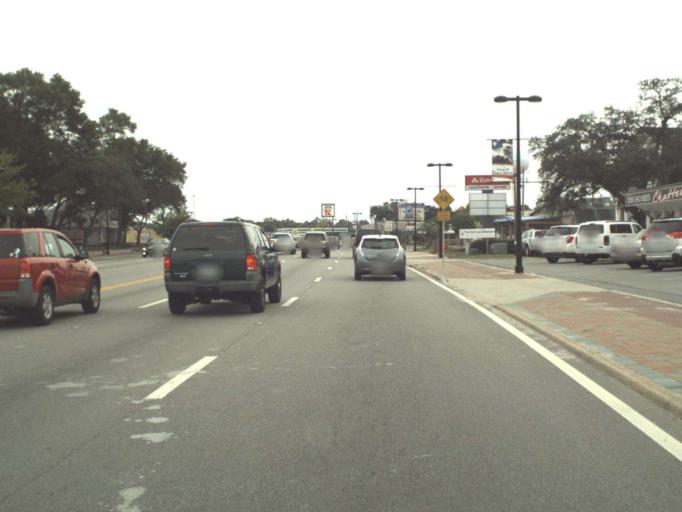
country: US
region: Florida
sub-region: Okaloosa County
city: Ocean City
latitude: 30.4236
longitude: -86.6096
